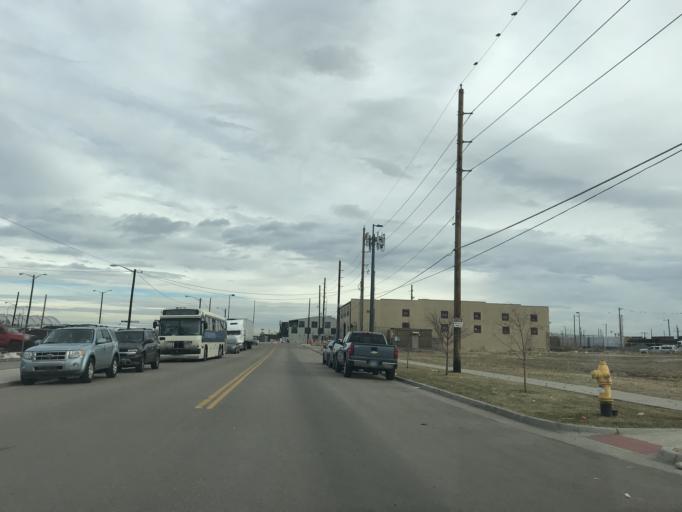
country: US
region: Colorado
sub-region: Denver County
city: Denver
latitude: 39.7731
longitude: -104.9736
